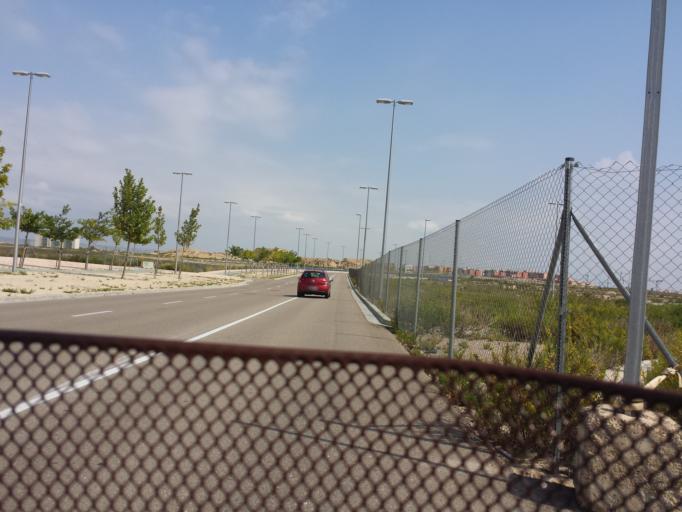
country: ES
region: Aragon
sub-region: Provincia de Zaragoza
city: Montecanal
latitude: 41.6277
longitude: -0.9560
